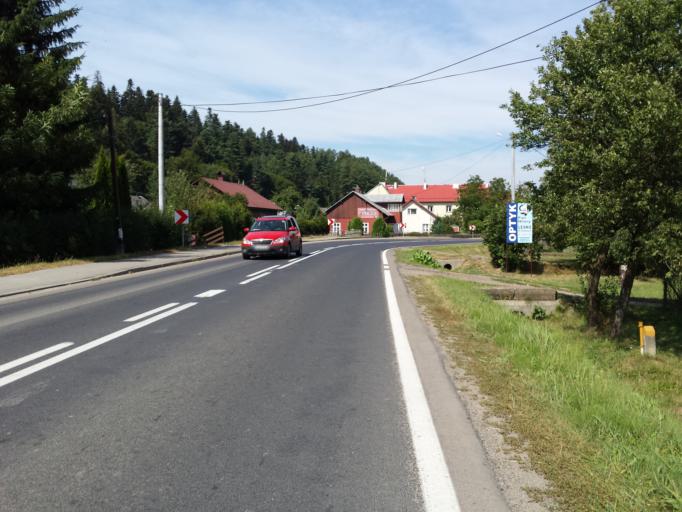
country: PL
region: Subcarpathian Voivodeship
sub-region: Powiat leski
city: Lesko
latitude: 49.4667
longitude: 22.3207
